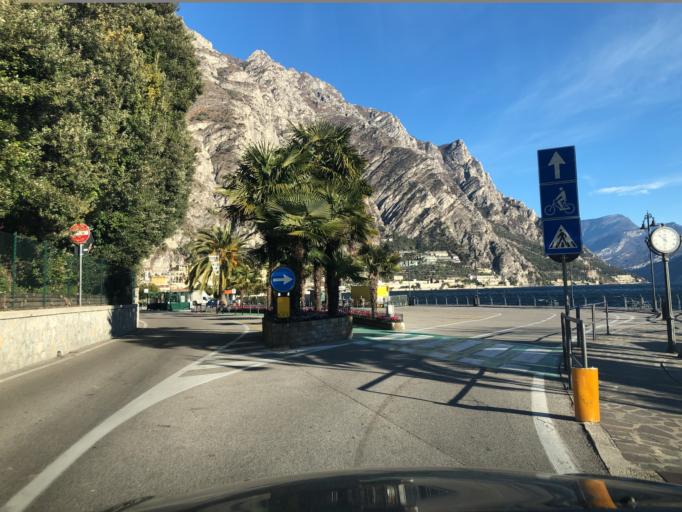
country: IT
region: Lombardy
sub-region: Provincia di Brescia
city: Limone sul Garda
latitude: 45.8112
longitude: 10.7937
